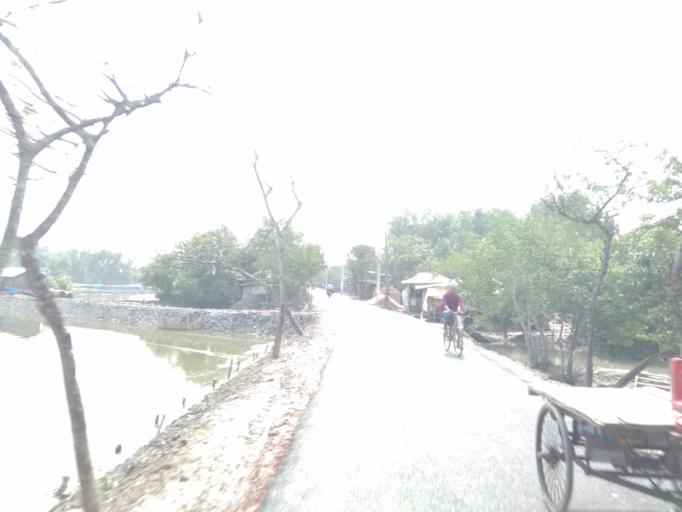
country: IN
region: West Bengal
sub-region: North 24 Parganas
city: Gosaba
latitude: 22.2655
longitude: 89.2187
